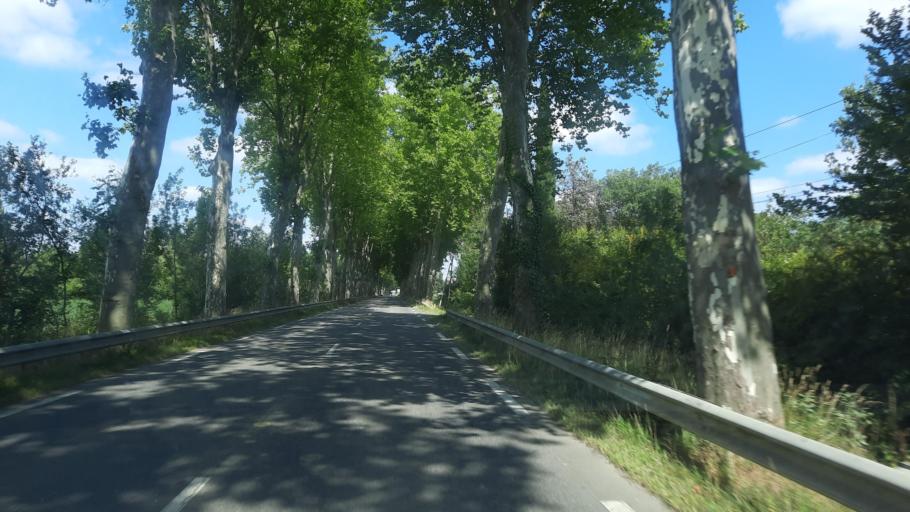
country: FR
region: Midi-Pyrenees
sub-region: Departement du Gers
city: Samatan
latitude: 43.4803
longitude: 0.9259
